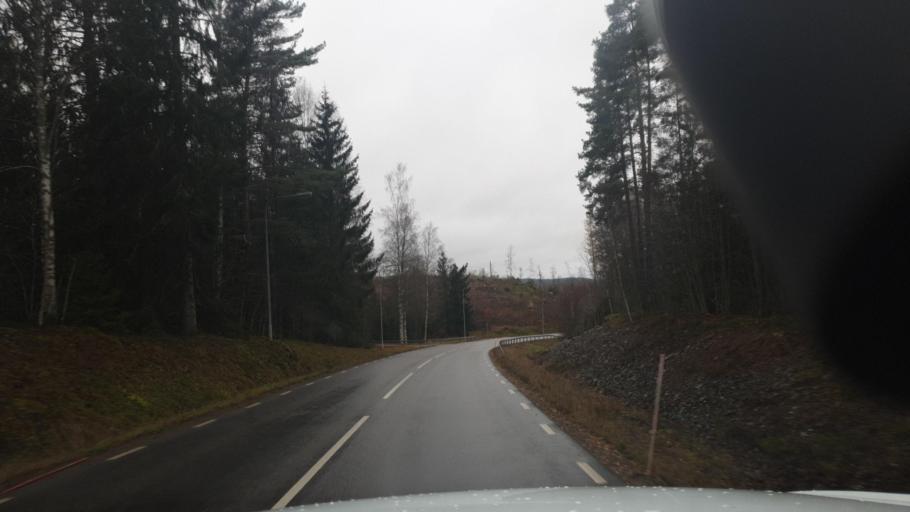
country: SE
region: Vaermland
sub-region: Arvika Kommun
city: Arvika
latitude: 59.5440
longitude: 12.5754
